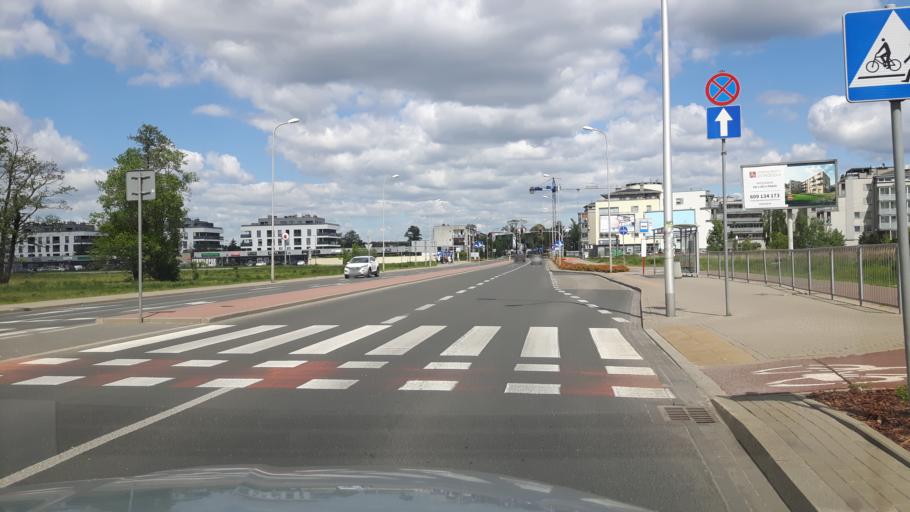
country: PL
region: Masovian Voivodeship
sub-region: Warszawa
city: Targowek
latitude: 52.3102
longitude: 21.0623
